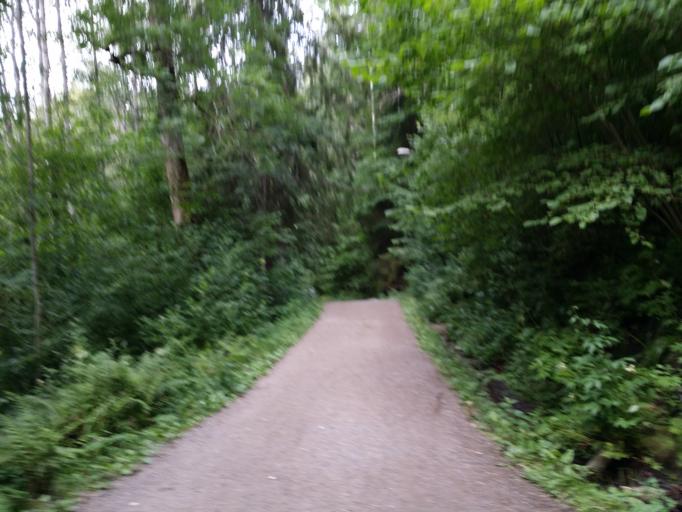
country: NO
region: Akershus
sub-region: Lorenskog
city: Kjenn
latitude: 59.8926
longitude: 10.8788
